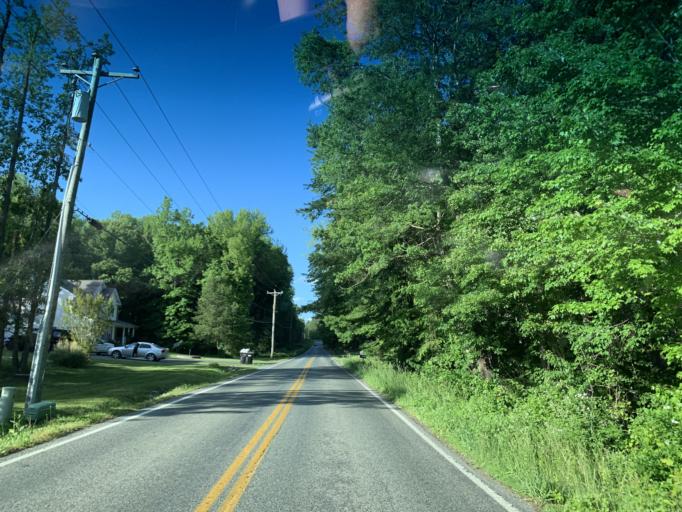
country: US
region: Maryland
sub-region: Cecil County
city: Elkton
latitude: 39.5851
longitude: -75.8718
